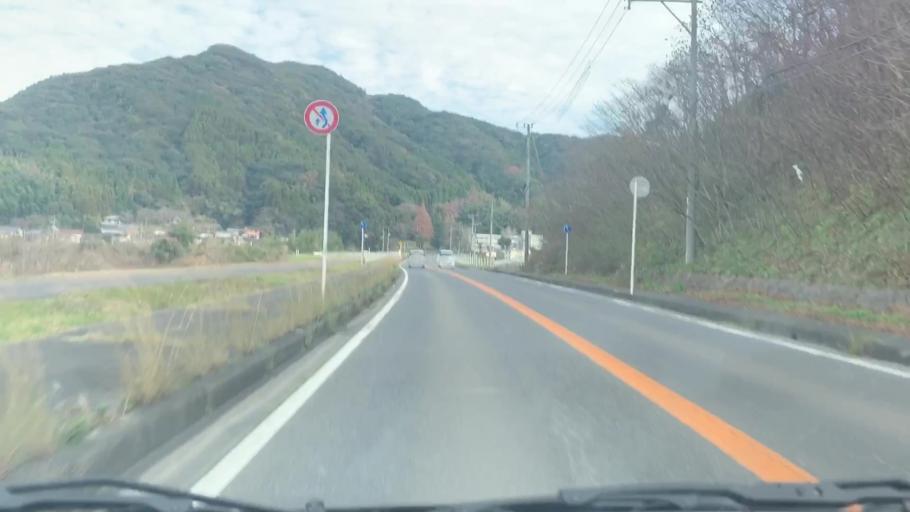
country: JP
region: Saga Prefecture
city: Karatsu
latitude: 33.3603
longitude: 130.0087
